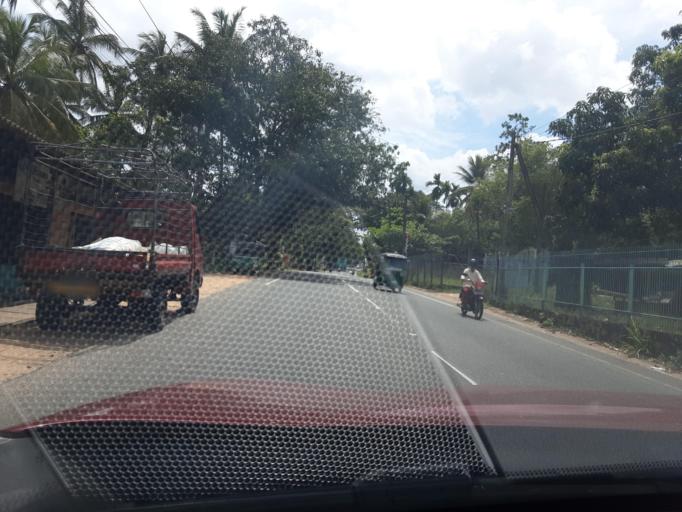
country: LK
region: North Western
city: Kuliyapitiya
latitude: 7.4513
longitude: 80.1924
